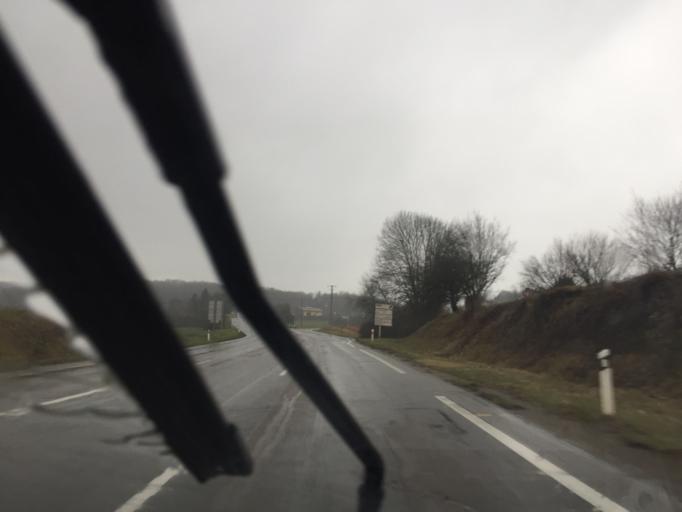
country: FR
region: Franche-Comte
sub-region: Departement du Jura
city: Mouchard
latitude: 46.9818
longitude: 5.8133
